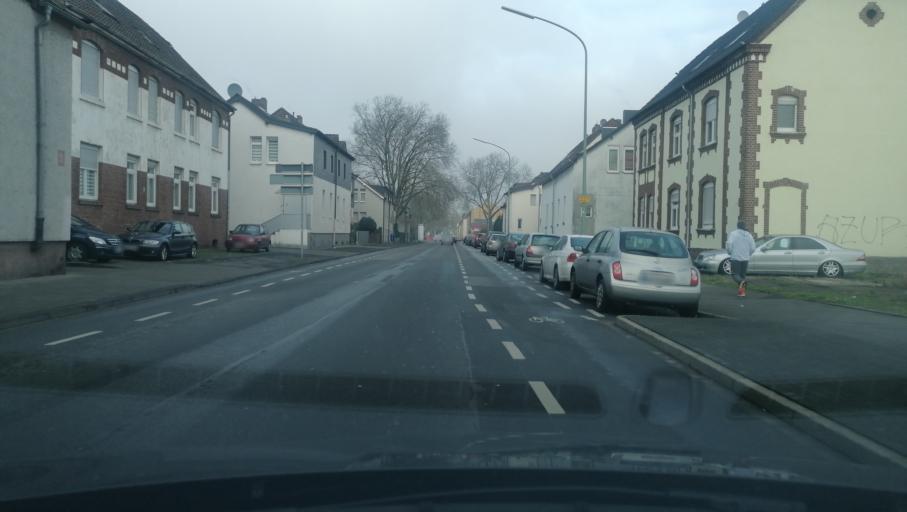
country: DE
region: North Rhine-Westphalia
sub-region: Regierungsbezirk Munster
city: Gelsenkirchen
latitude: 51.5095
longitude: 7.1128
